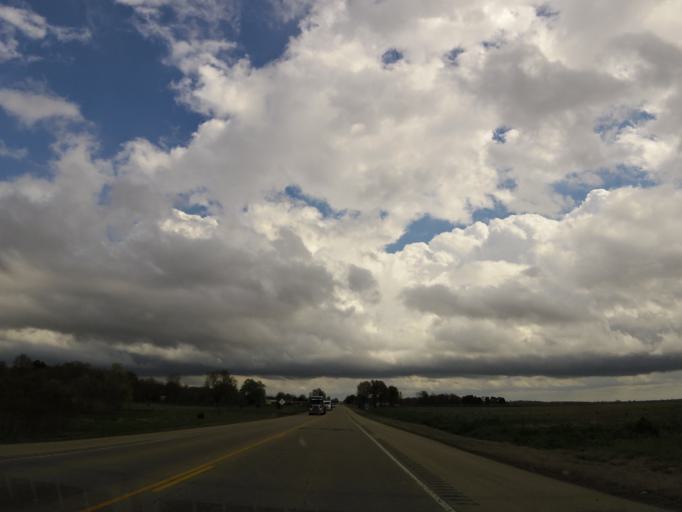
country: US
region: Arkansas
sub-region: Clay County
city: Corning
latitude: 36.4571
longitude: -90.5817
